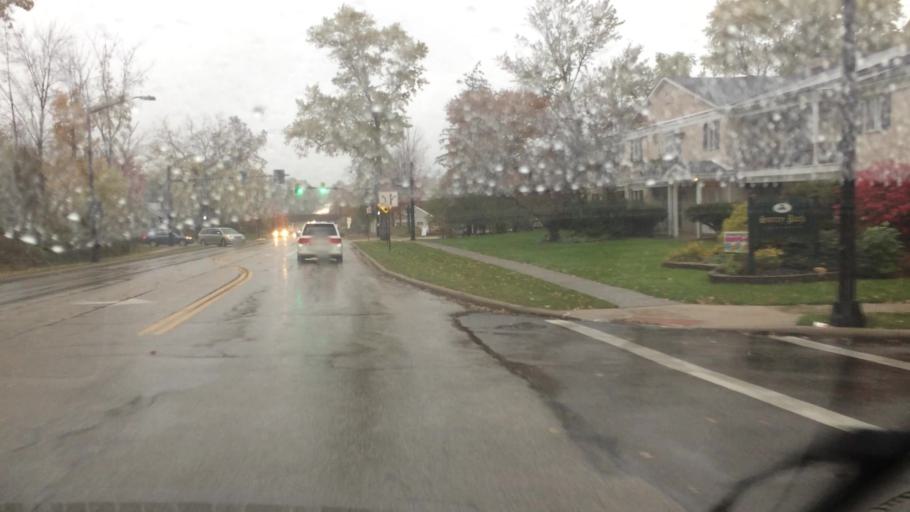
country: US
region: Ohio
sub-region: Summit County
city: Hudson
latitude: 41.2353
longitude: -81.4403
